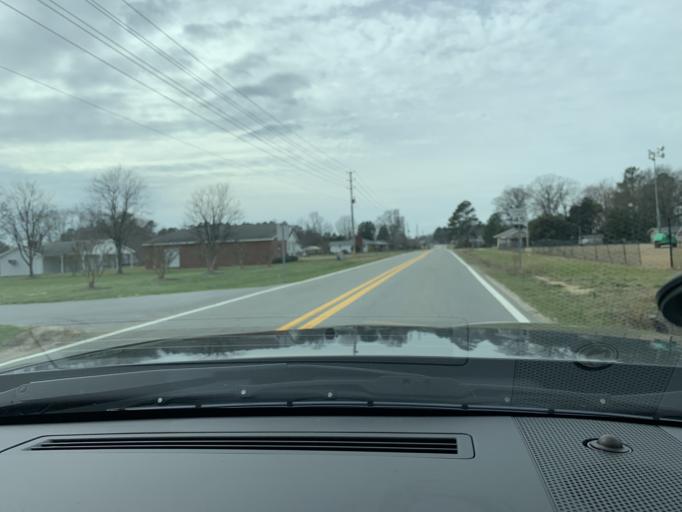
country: US
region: North Carolina
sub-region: Johnston County
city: Clayton
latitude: 35.6150
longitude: -78.4123
